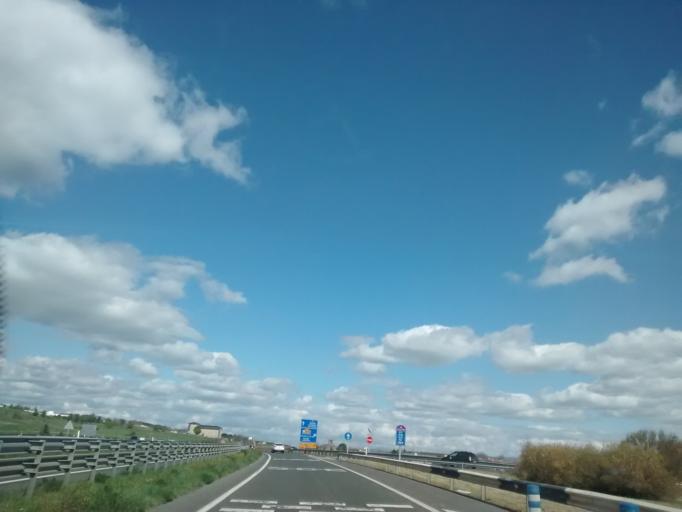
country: ES
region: Basque Country
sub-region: Provincia de Alava
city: Gasteiz / Vitoria
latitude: 42.8801
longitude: -2.6970
